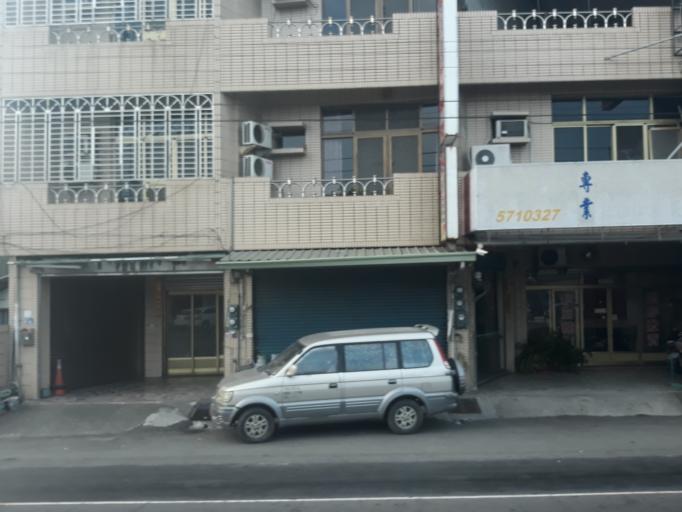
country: TW
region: Taiwan
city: Xinying
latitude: 23.1843
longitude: 120.2393
